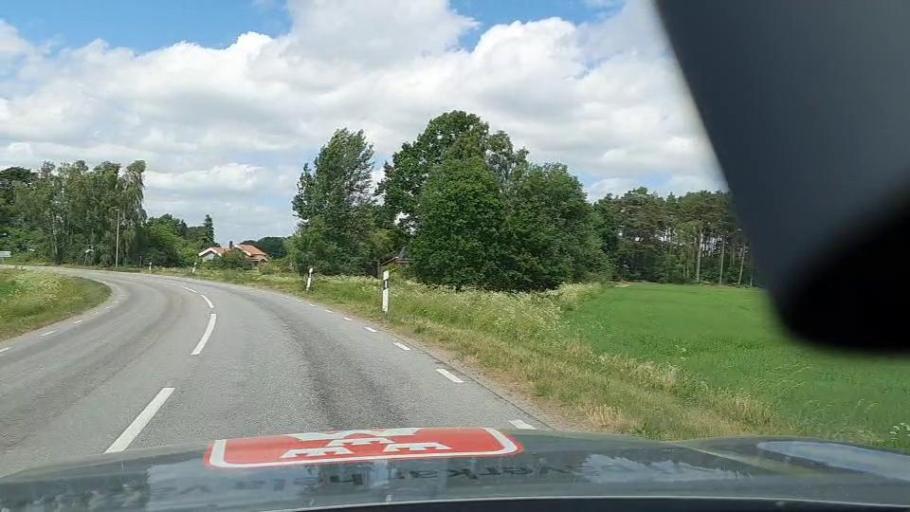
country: SE
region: Blekinge
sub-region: Karlshamns Kommun
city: Morrum
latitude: 56.0896
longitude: 14.7060
